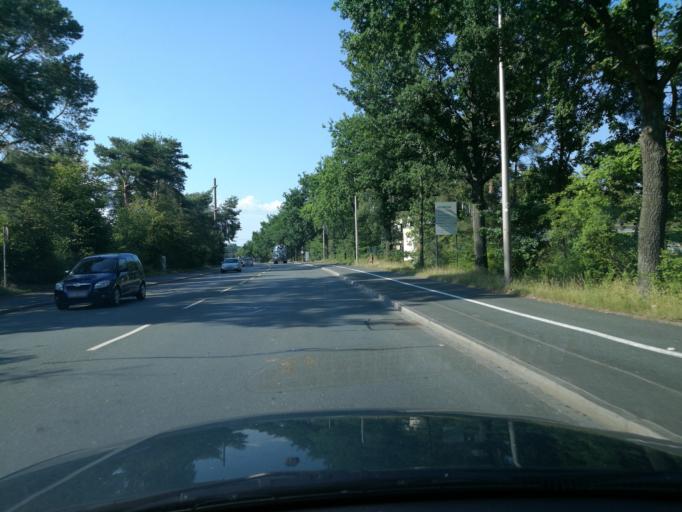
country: DE
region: Bavaria
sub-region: Regierungsbezirk Mittelfranken
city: Erlangen
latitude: 49.5781
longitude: 10.9675
